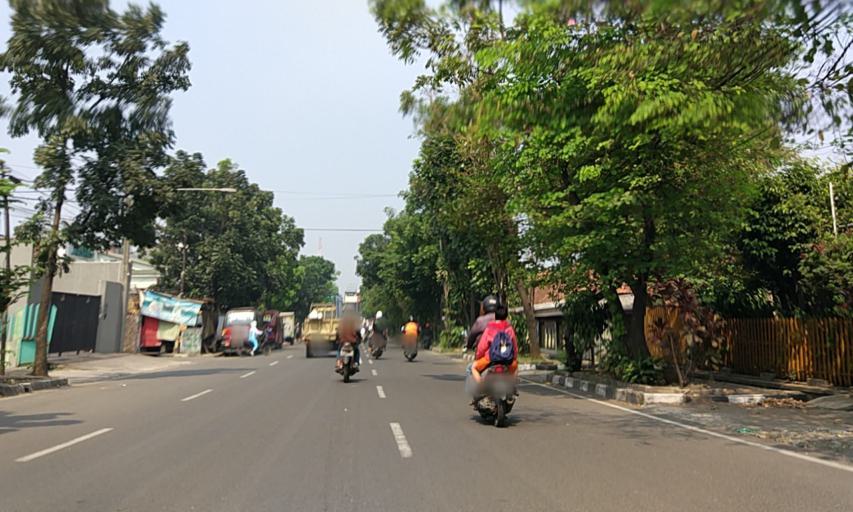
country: ID
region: West Java
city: Bandung
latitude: -6.9150
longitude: 107.5773
